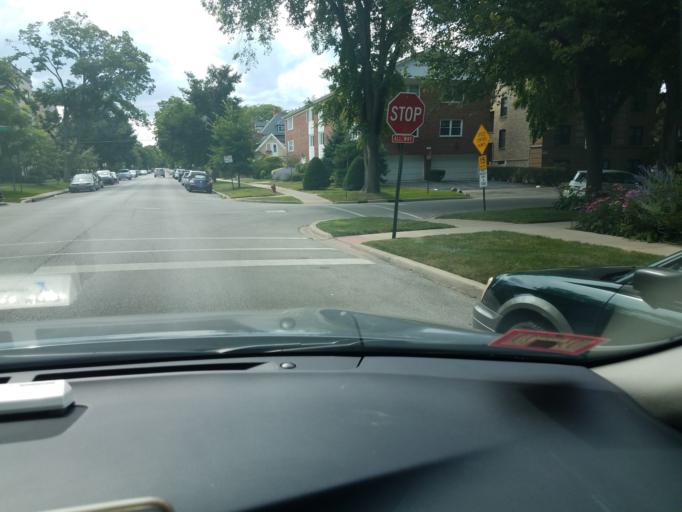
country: US
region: Illinois
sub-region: Cook County
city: Evanston
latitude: 42.0427
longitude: -87.6834
